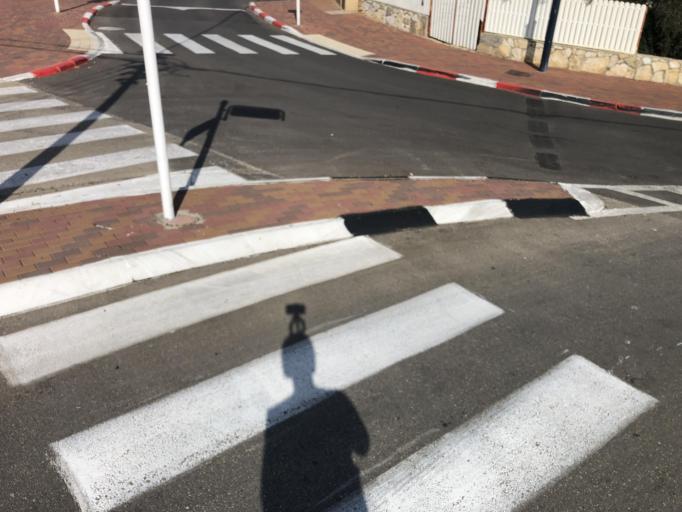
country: IL
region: Northern District
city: `Akko
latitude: 32.9359
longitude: 35.0936
